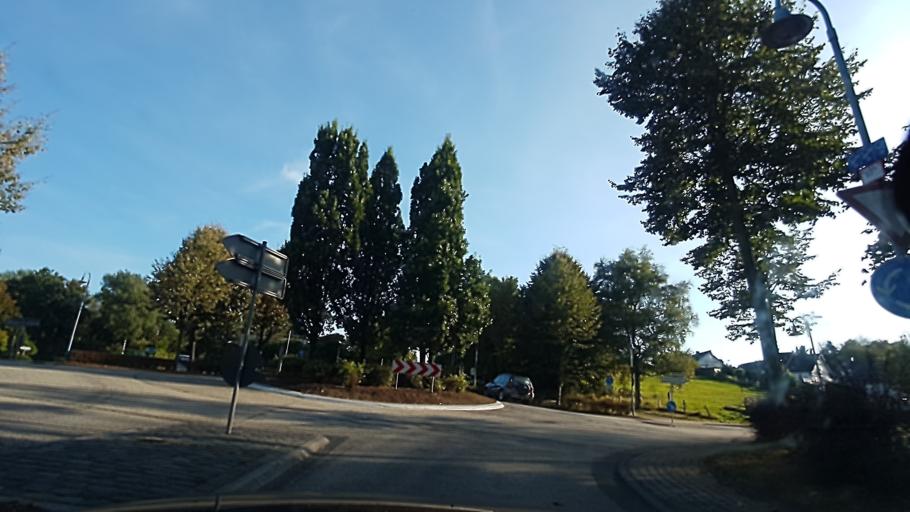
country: DE
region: North Rhine-Westphalia
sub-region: Regierungsbezirk Koln
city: Marienheide
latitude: 51.0877
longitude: 7.5293
